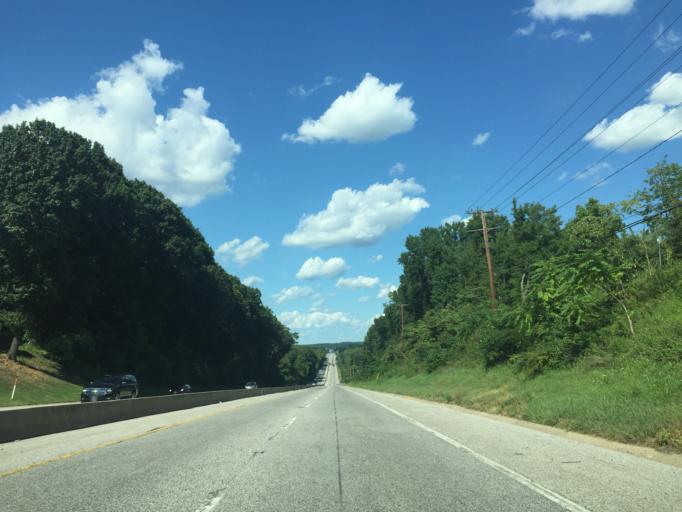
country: US
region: Maryland
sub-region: Baltimore County
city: White Marsh
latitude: 39.4007
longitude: -76.4006
